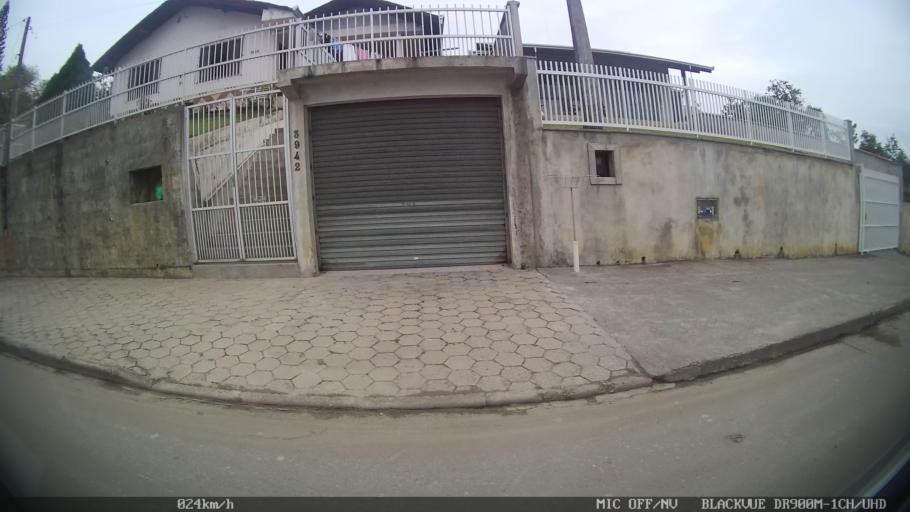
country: BR
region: Santa Catarina
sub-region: Joinville
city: Joinville
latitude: -26.3516
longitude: -48.7967
